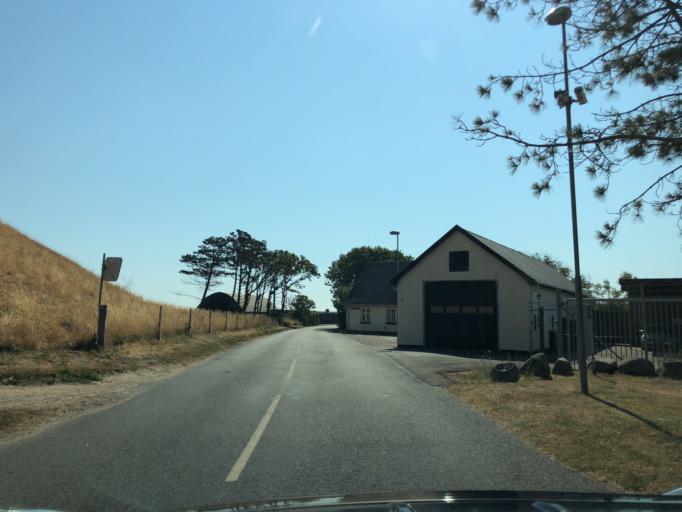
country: DK
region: Zealand
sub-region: Odsherred Kommune
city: Asnaes
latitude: 56.0052
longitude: 11.2813
